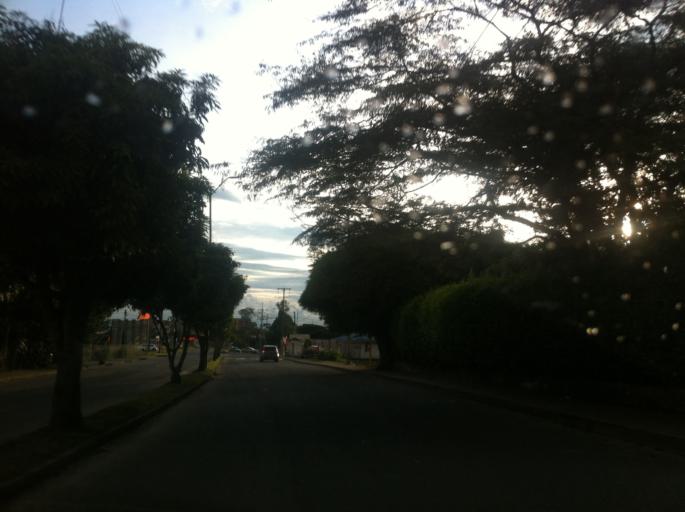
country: CO
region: Quindio
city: Calarca
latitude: 4.5605
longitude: -75.6468
